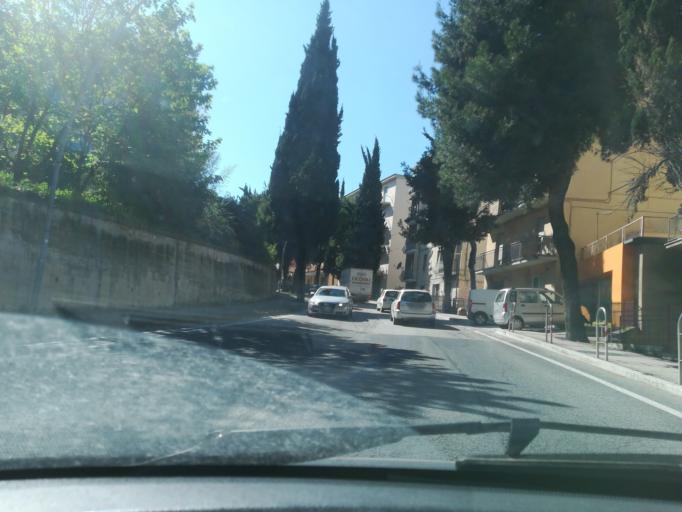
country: IT
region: The Marches
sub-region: Provincia di Macerata
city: Macerata
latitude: 43.2955
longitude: 13.4618
